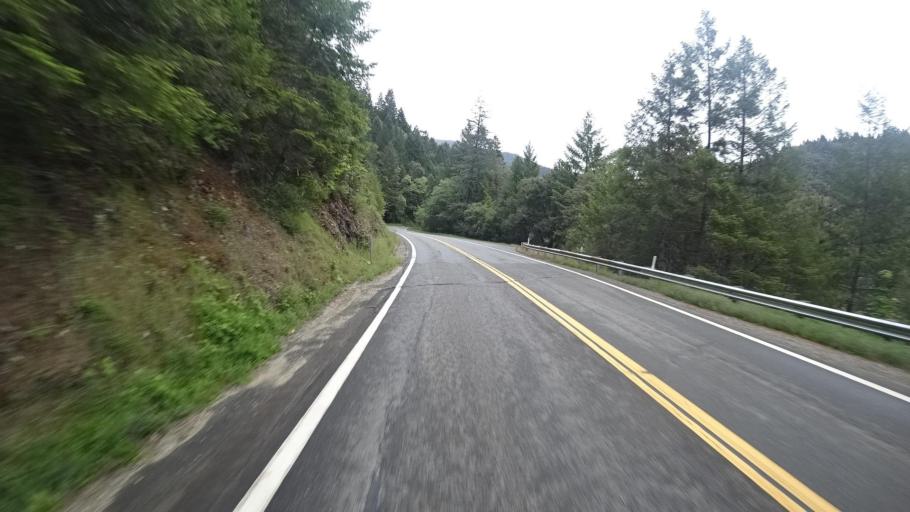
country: US
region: California
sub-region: Humboldt County
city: Willow Creek
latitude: 41.2660
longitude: -123.6062
